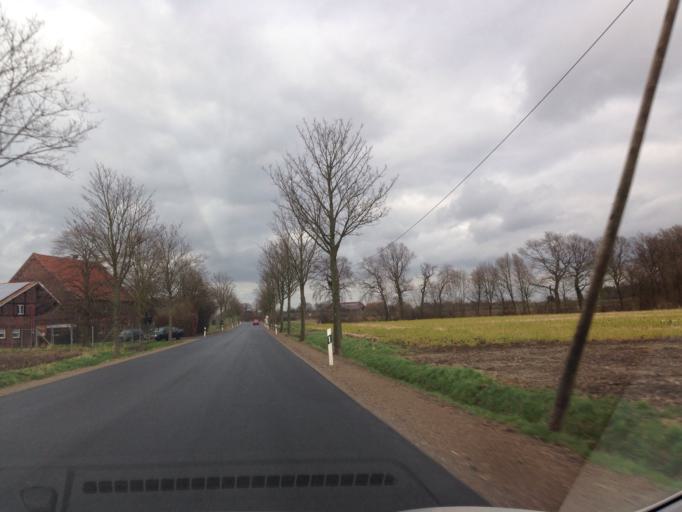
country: DE
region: North Rhine-Westphalia
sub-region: Regierungsbezirk Munster
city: Nordkirchen
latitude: 51.7687
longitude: 7.5405
